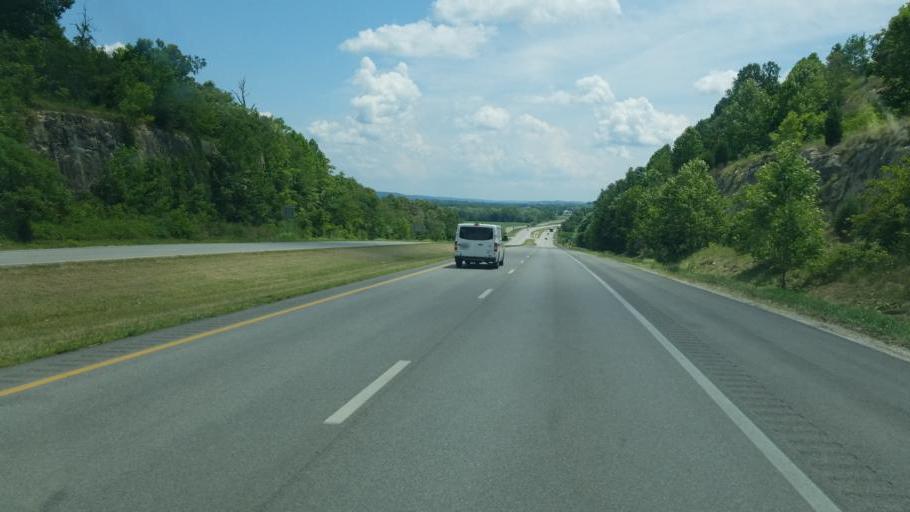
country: US
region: West Virginia
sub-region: Mason County
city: Point Pleasant
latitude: 38.8213
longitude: -82.1232
